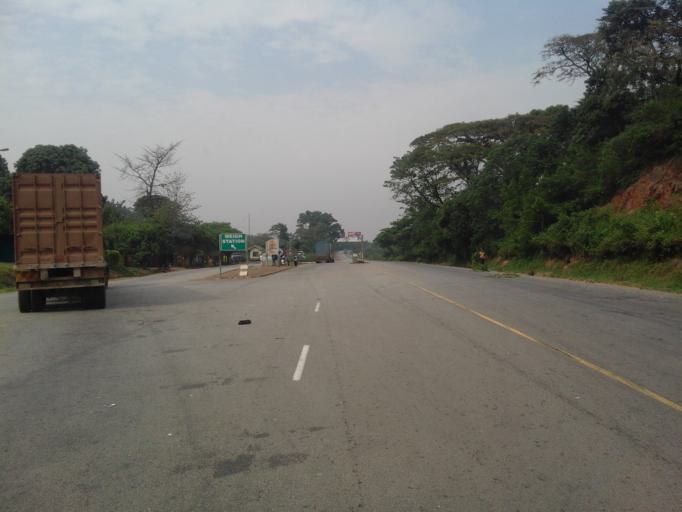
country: UG
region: Eastern Region
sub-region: Busia District
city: Busia
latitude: 0.5250
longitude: 33.9677
